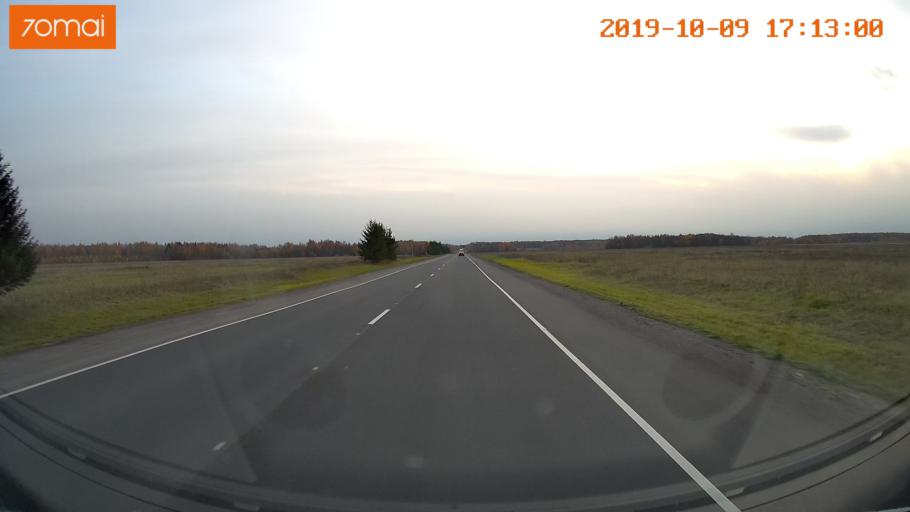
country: RU
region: Ivanovo
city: Privolzhsk
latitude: 57.3209
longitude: 41.2317
